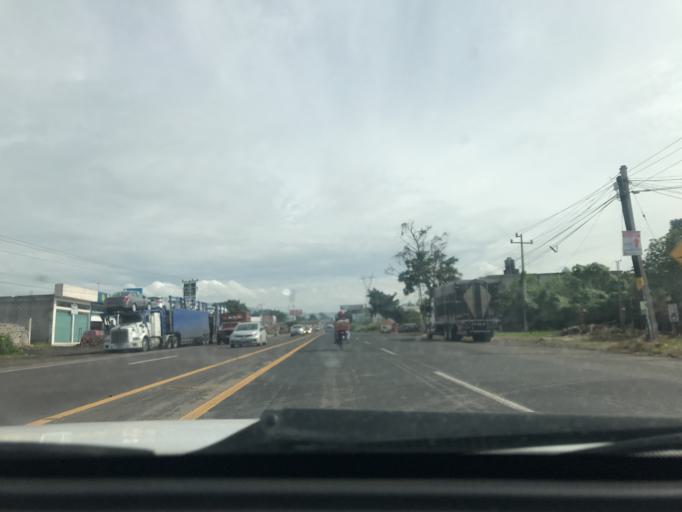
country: MX
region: Morelos
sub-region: Atlatlahucan
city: Colonia San Francisco
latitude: 18.8900
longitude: -98.9136
